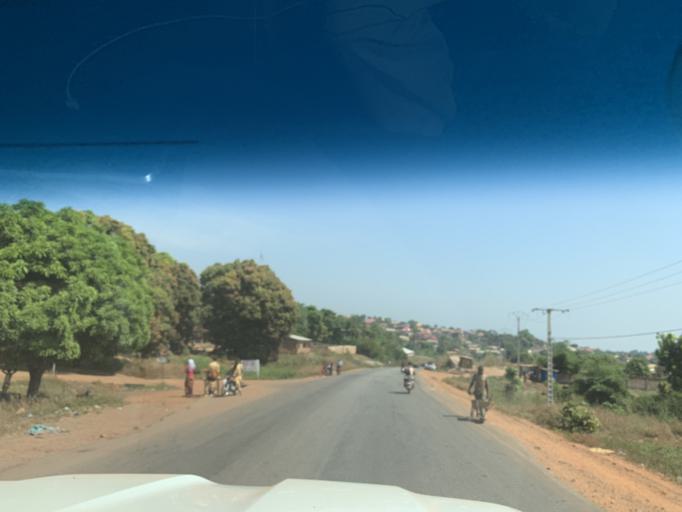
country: GN
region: Kindia
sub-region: Kindia
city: Kindia
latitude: 10.0295
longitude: -12.8728
